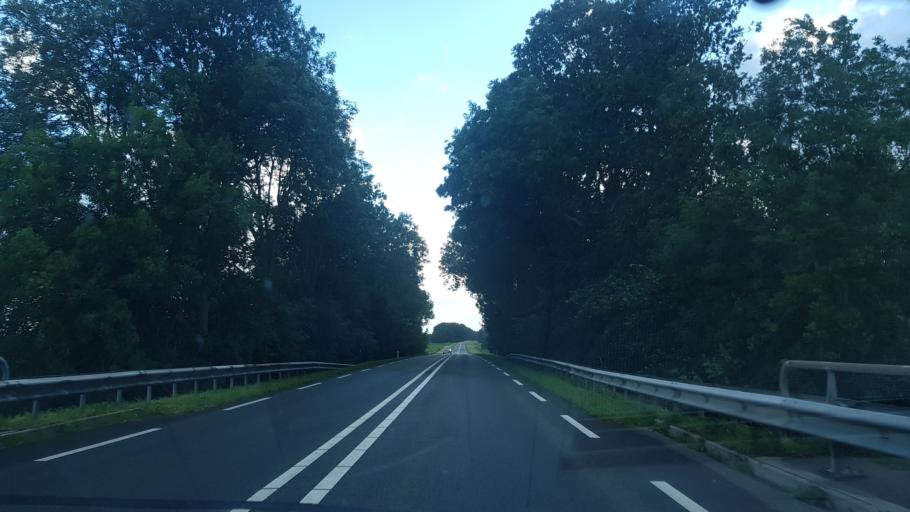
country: NL
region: Groningen
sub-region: Gemeente Slochteren
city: Slochteren
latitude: 53.3096
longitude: 6.7492
